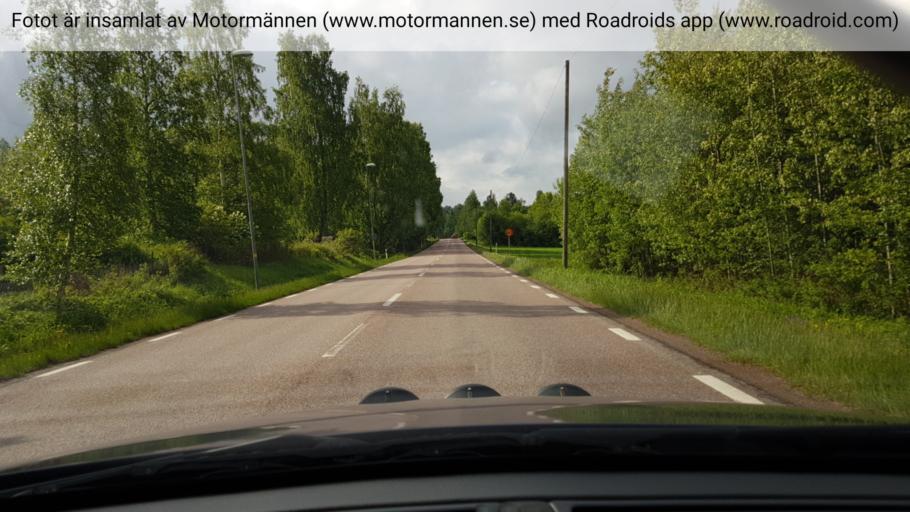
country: SE
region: Dalarna
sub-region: Orsa Kommun
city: Orsa
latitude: 61.1053
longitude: 14.6324
